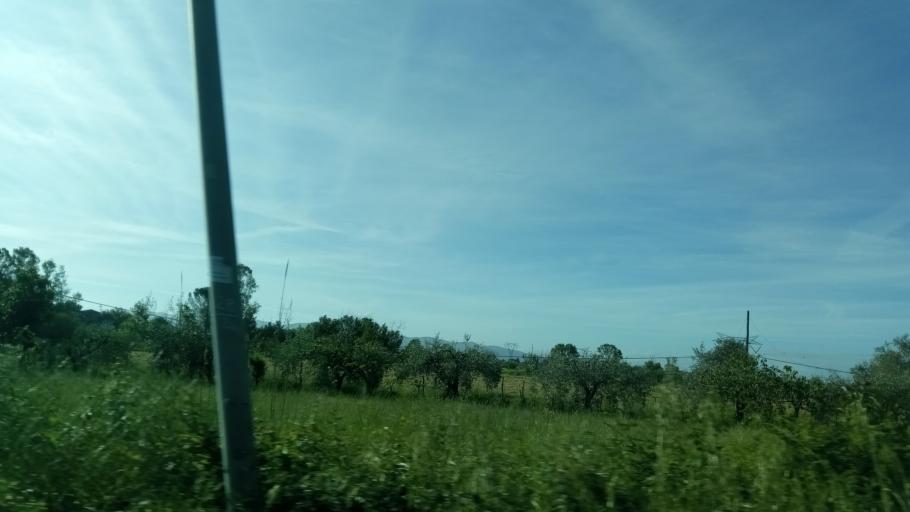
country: IT
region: Latium
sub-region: Provincia di Latina
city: Grunuovo-Campomaggiore San Luca
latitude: 41.2687
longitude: 13.7868
